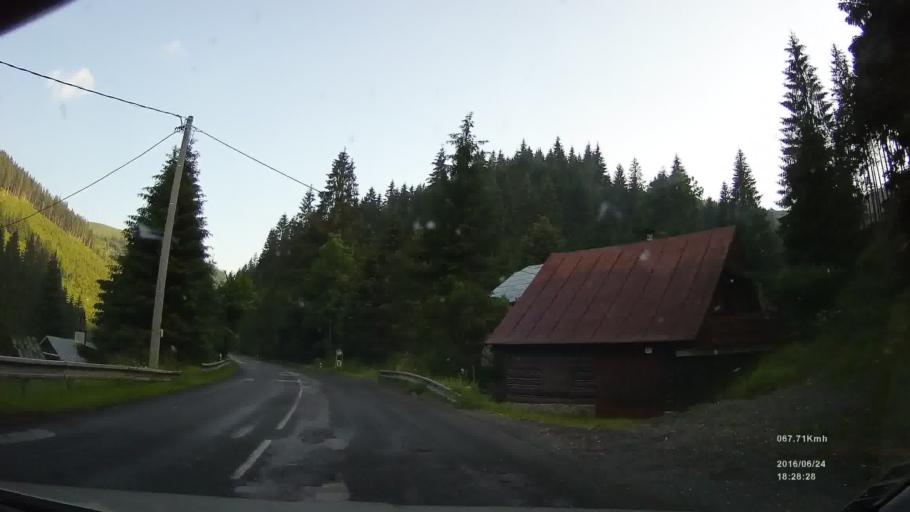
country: SK
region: Zilinsky
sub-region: Okres Zilina
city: Liptovsky Hradok
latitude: 48.9413
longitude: 19.7569
